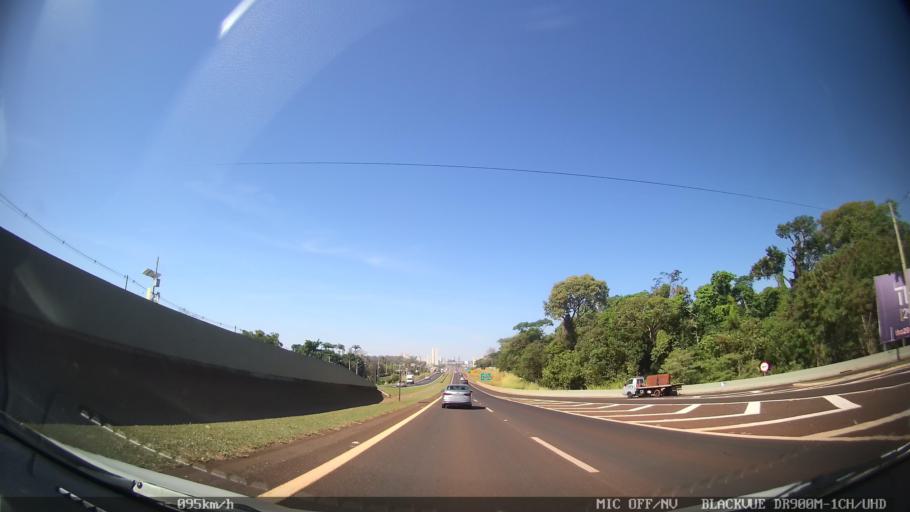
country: BR
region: Sao Paulo
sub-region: Ribeirao Preto
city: Ribeirao Preto
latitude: -21.2117
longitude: -47.8461
